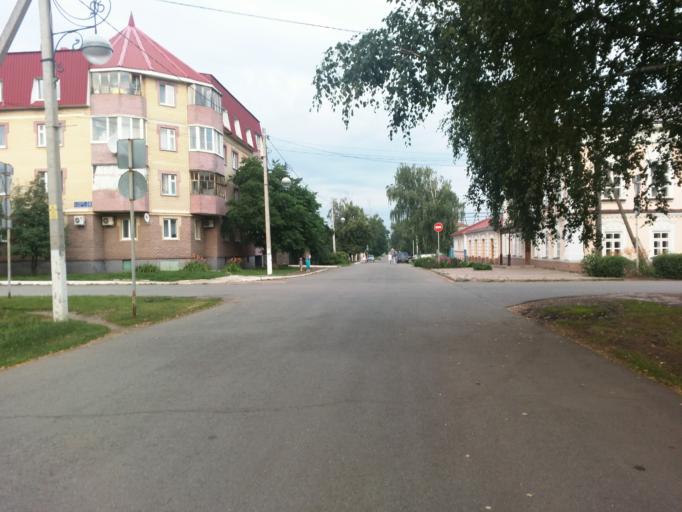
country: RU
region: Tatarstan
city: Yelabuga
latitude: 55.7548
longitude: 52.0687
